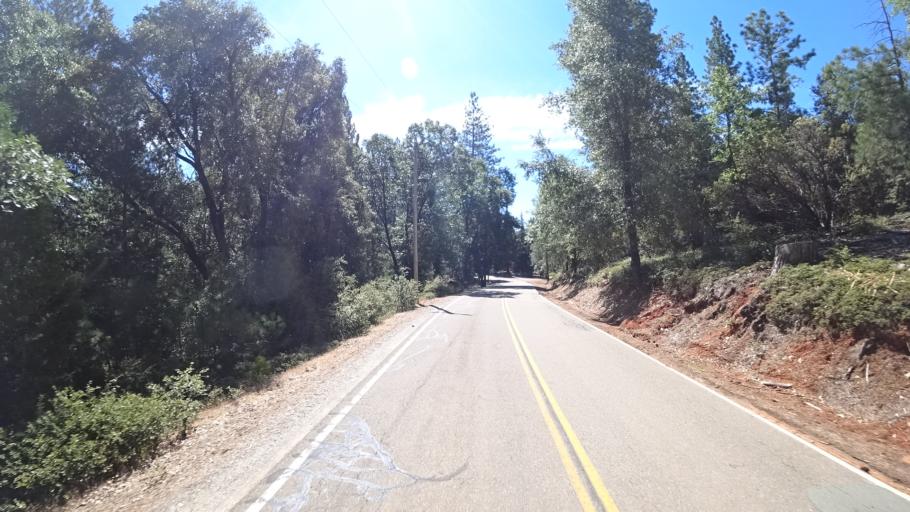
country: US
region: California
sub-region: Amador County
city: Pioneer
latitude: 38.3365
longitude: -120.5362
